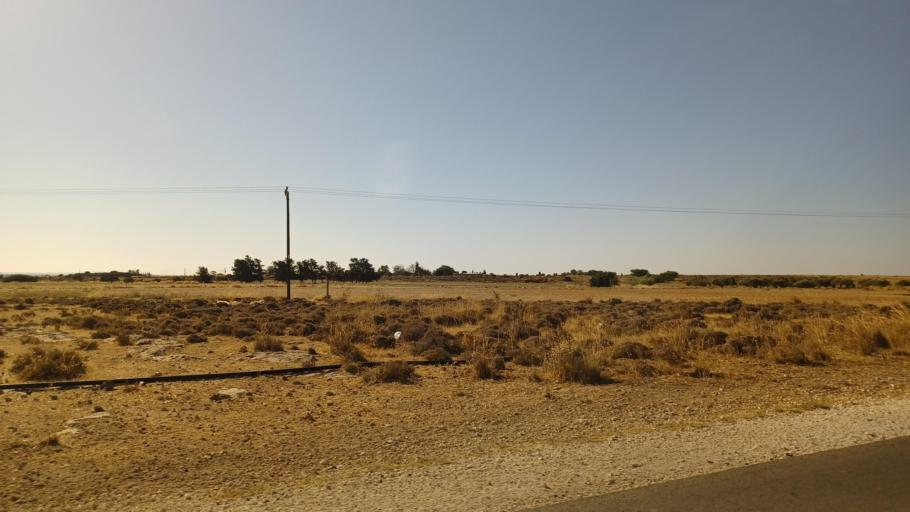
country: CY
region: Larnaka
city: Pergamos
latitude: 35.0274
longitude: 33.7047
